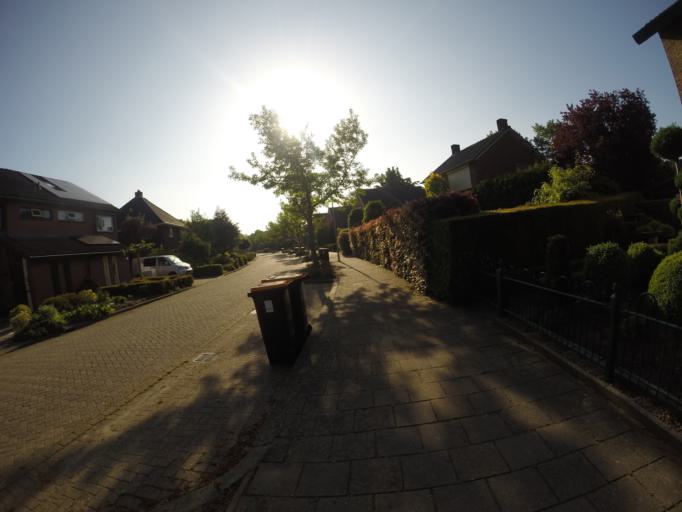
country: NL
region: Gelderland
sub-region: Oude IJsselstreek
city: Gendringen
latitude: 51.9314
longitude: 6.3514
